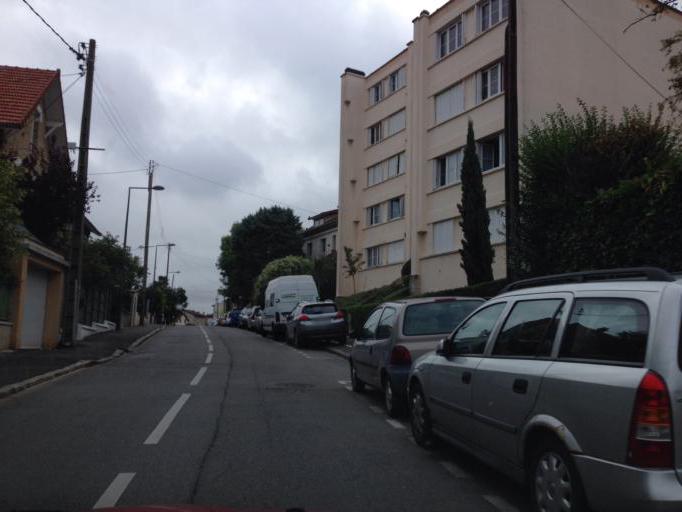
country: FR
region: Ile-de-France
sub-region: Departement des Hauts-de-Seine
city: Meudon
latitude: 48.8093
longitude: 2.2446
